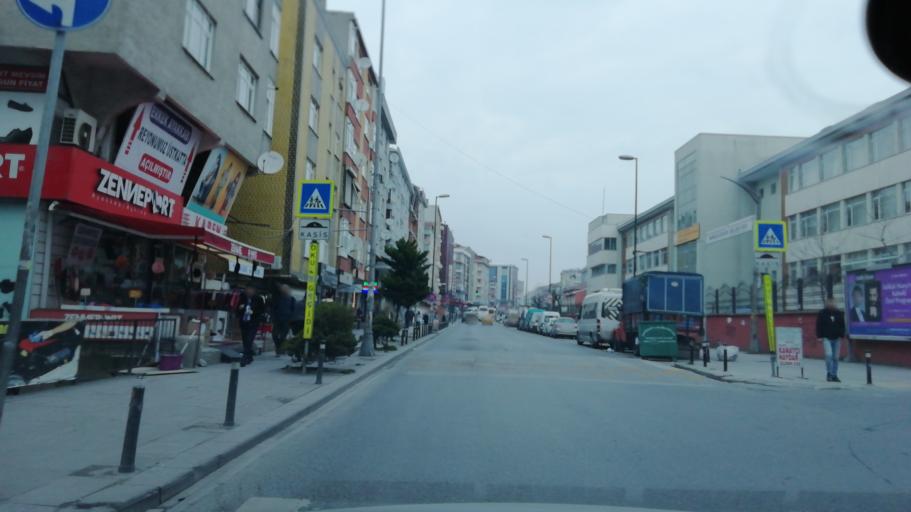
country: TR
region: Istanbul
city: Bahcelievler
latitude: 41.0109
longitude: 28.8415
